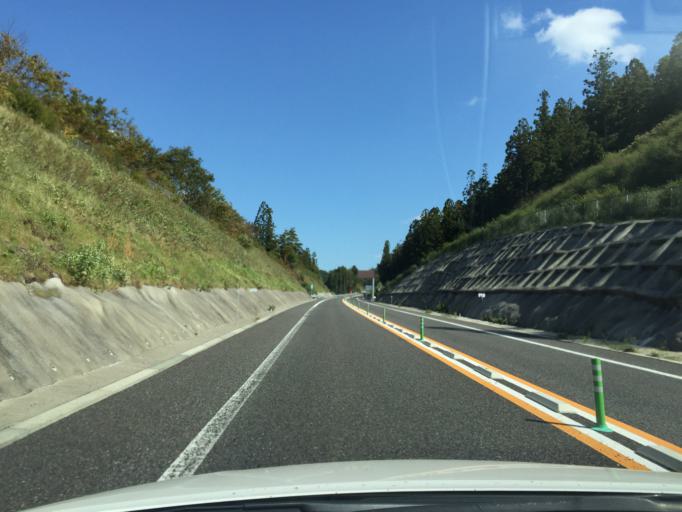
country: JP
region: Fukushima
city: Ishikawa
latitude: 37.2079
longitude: 140.5287
